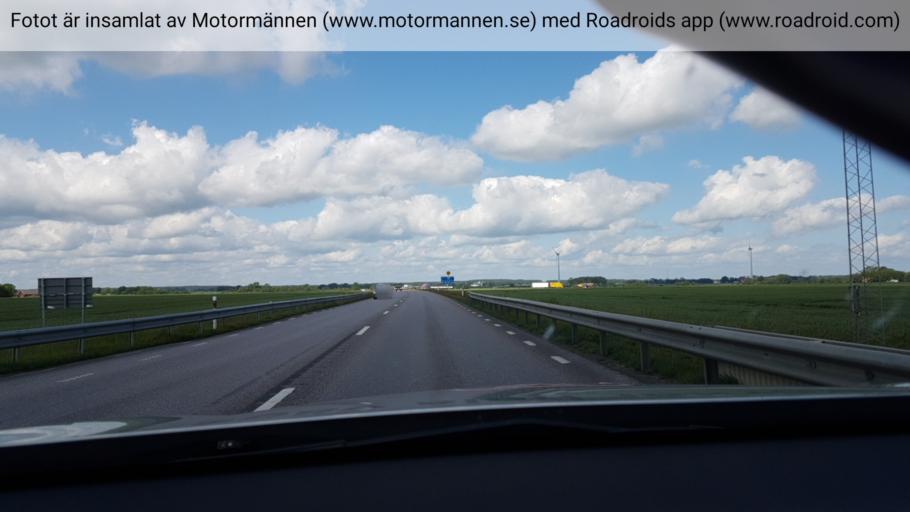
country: SE
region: Vaestra Goetaland
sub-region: Vara Kommun
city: Vara
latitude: 58.2948
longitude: 12.9611
